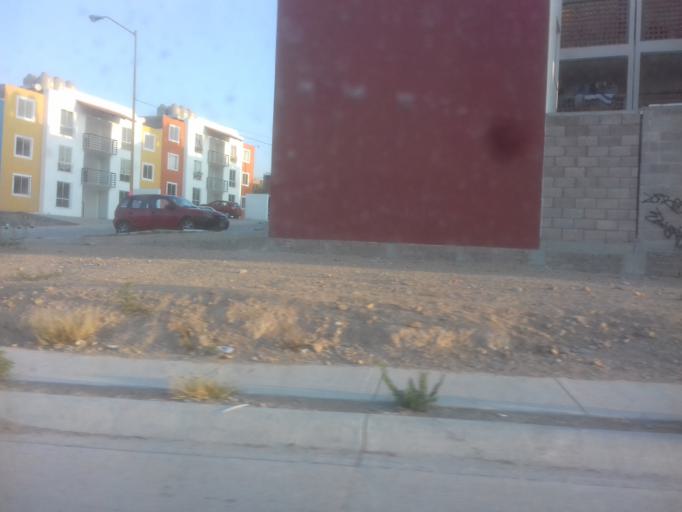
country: MX
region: Aguascalientes
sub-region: Aguascalientes
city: San Sebastian [Fraccionamiento]
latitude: 21.8494
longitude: -102.2610
